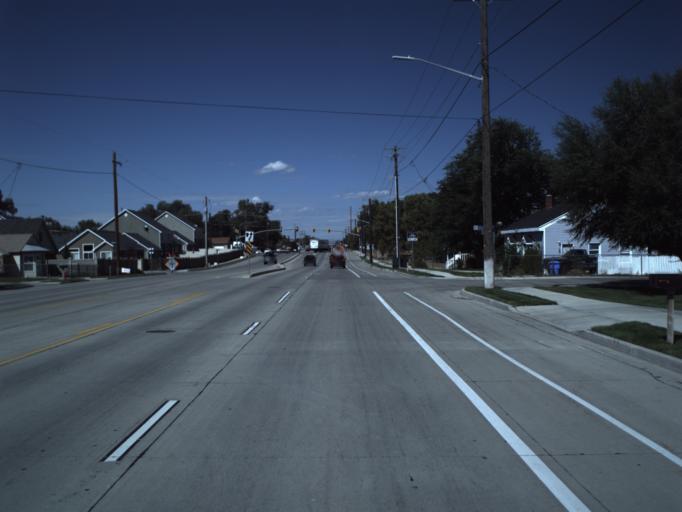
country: US
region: Utah
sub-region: Salt Lake County
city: Riverton
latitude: 40.5345
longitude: -111.9386
